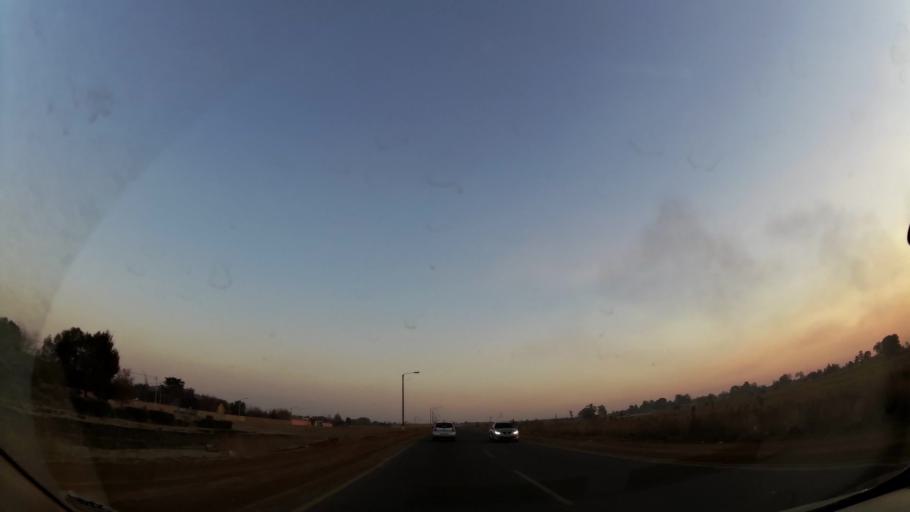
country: ZA
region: Gauteng
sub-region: Ekurhuleni Metropolitan Municipality
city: Springs
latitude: -26.3436
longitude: 28.4172
